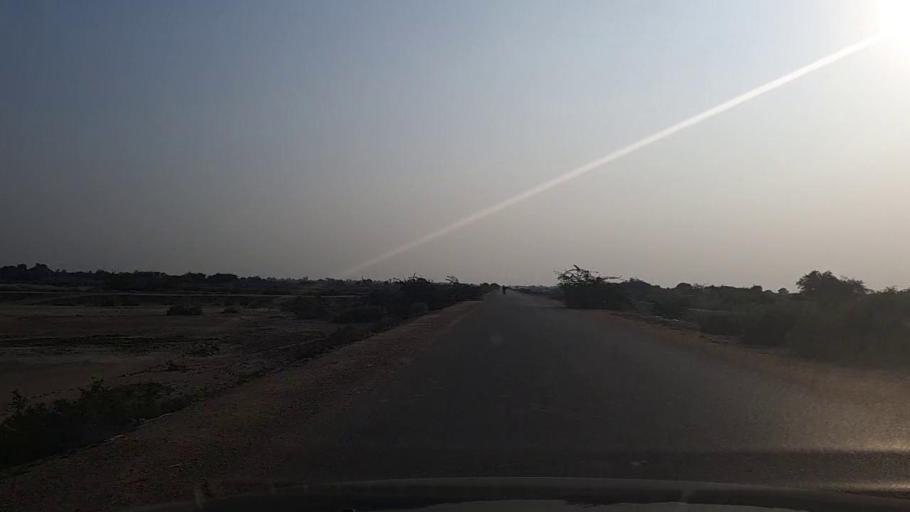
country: PK
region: Sindh
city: Mirpur Sakro
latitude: 24.5172
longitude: 67.8217
